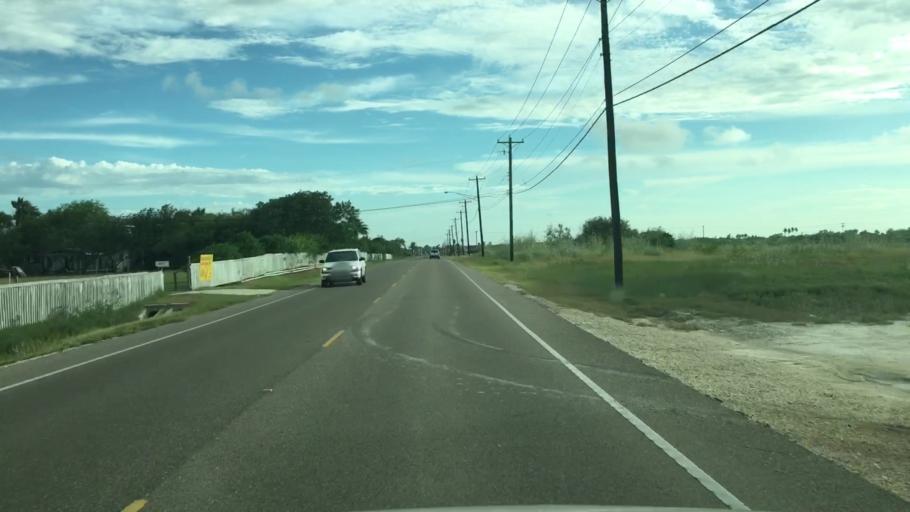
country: US
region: Texas
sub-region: Nueces County
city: Corpus Christi
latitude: 27.6471
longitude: -97.2825
